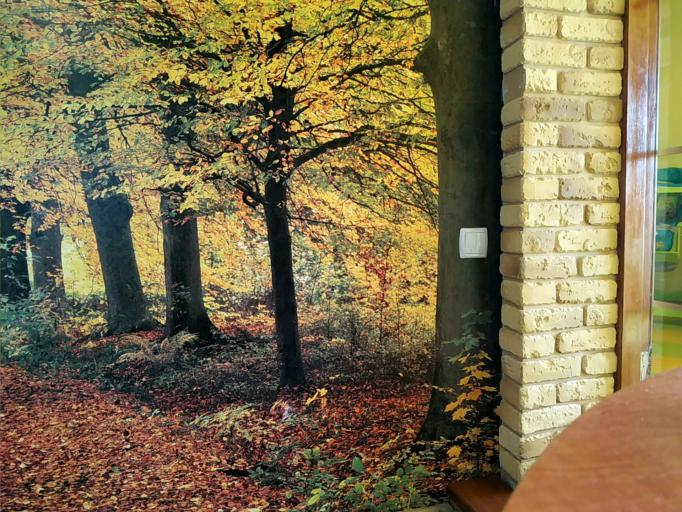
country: RU
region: Novgorod
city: Staraya Russa
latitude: 57.8324
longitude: 31.4856
